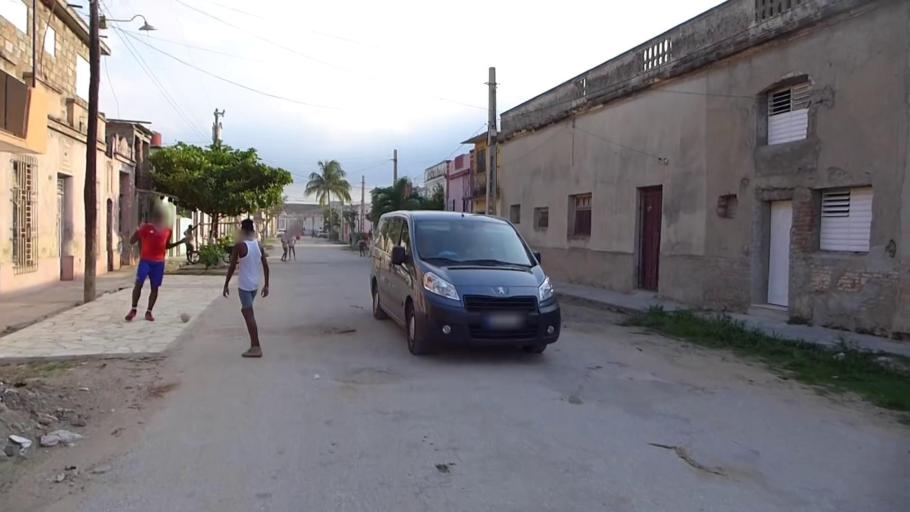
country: CU
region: Camaguey
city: Camaguey
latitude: 21.3855
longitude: -77.9100
